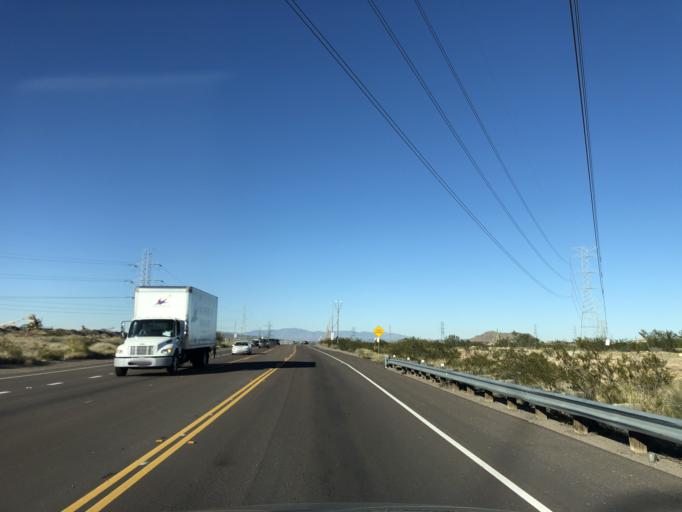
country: US
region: Arizona
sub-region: Maricopa County
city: Sun City West
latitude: 33.6968
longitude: -112.2896
